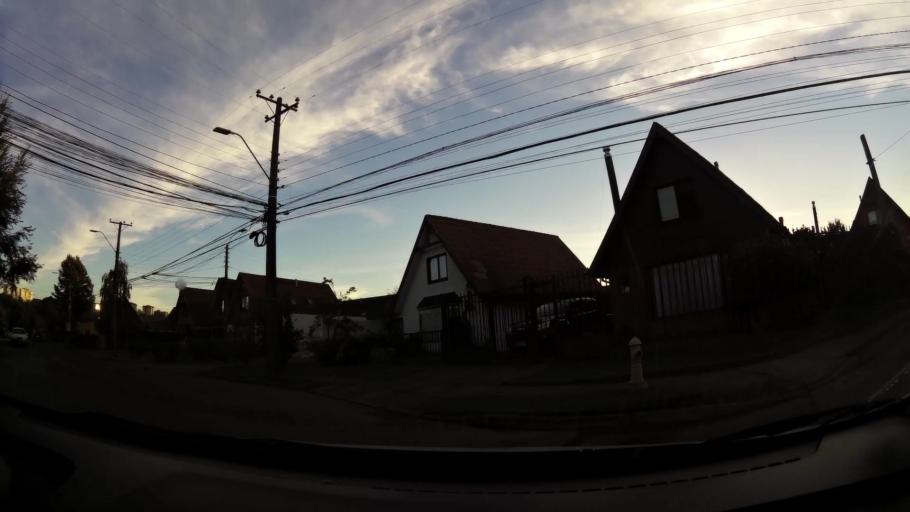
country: CL
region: Biobio
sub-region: Provincia de Concepcion
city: Concepcion
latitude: -36.8404
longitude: -73.0983
